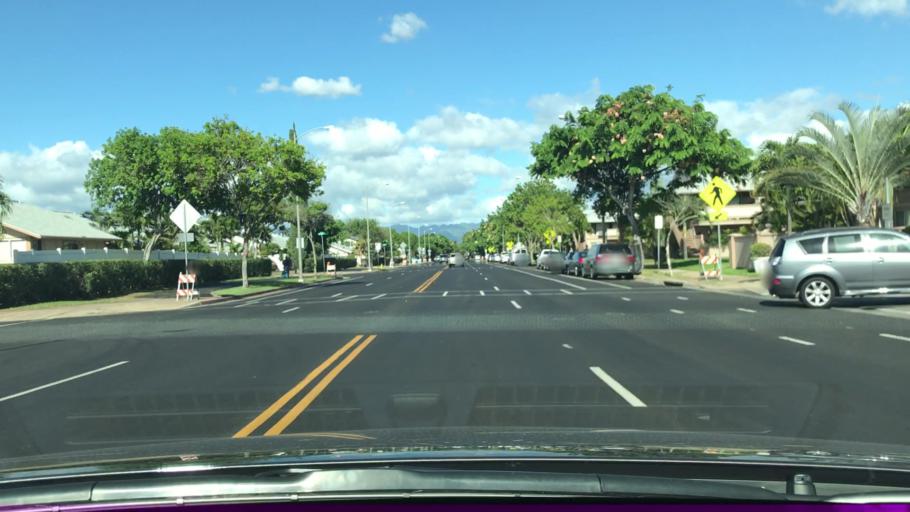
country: US
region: Hawaii
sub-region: Honolulu County
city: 'Ewa Gentry
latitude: 21.3392
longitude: -158.0306
